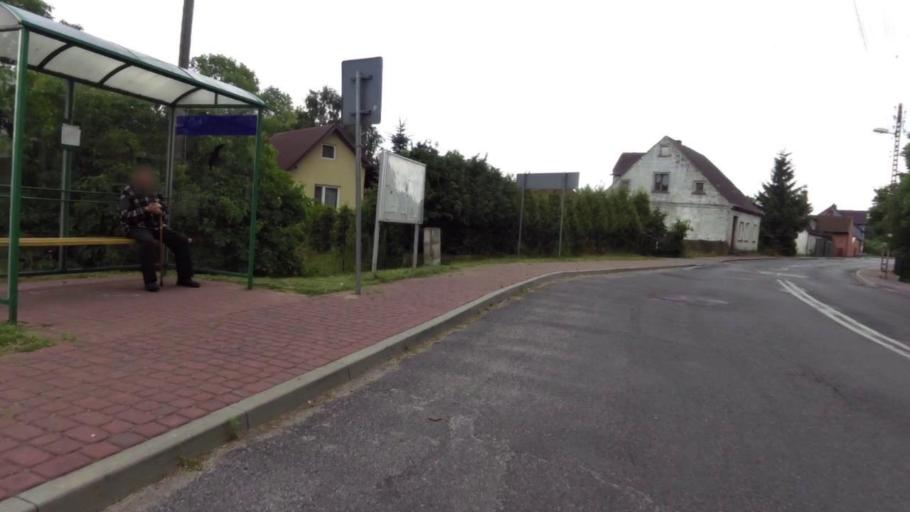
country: PL
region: West Pomeranian Voivodeship
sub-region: Powiat goleniowski
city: Stepnica
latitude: 53.6588
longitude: 14.6184
